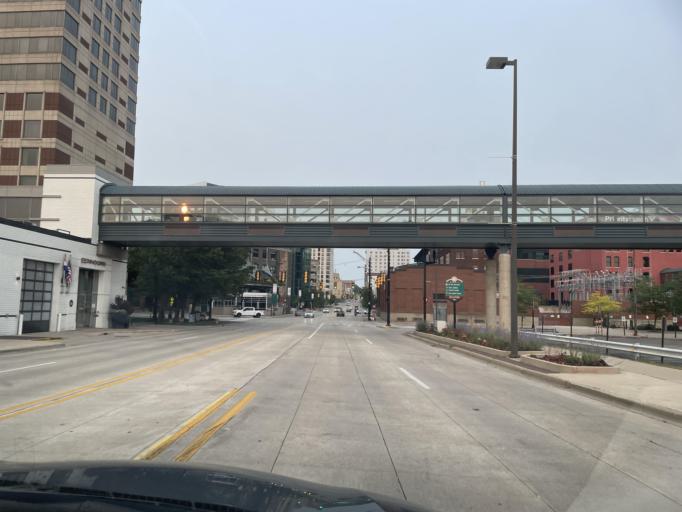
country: US
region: Michigan
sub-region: Kent County
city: Grand Rapids
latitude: 42.9632
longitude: -85.6745
